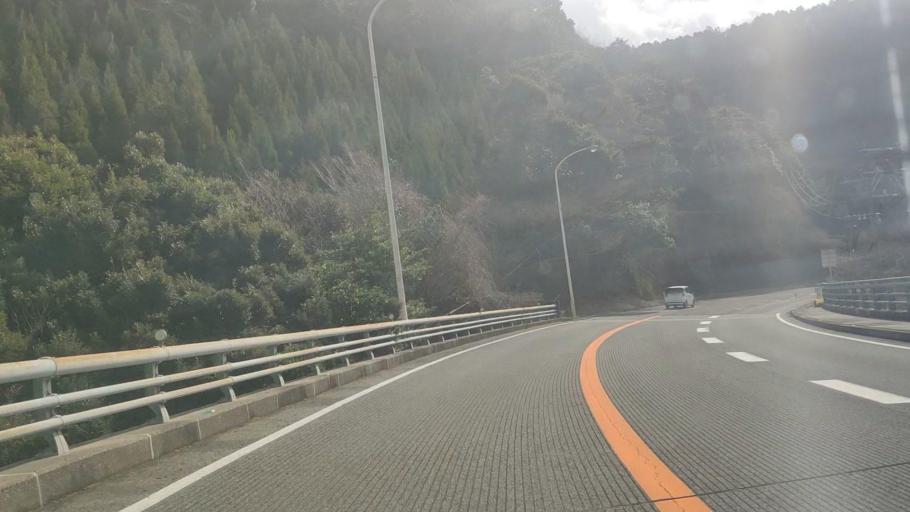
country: JP
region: Kumamoto
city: Hitoyoshi
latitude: 32.0787
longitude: 130.8031
